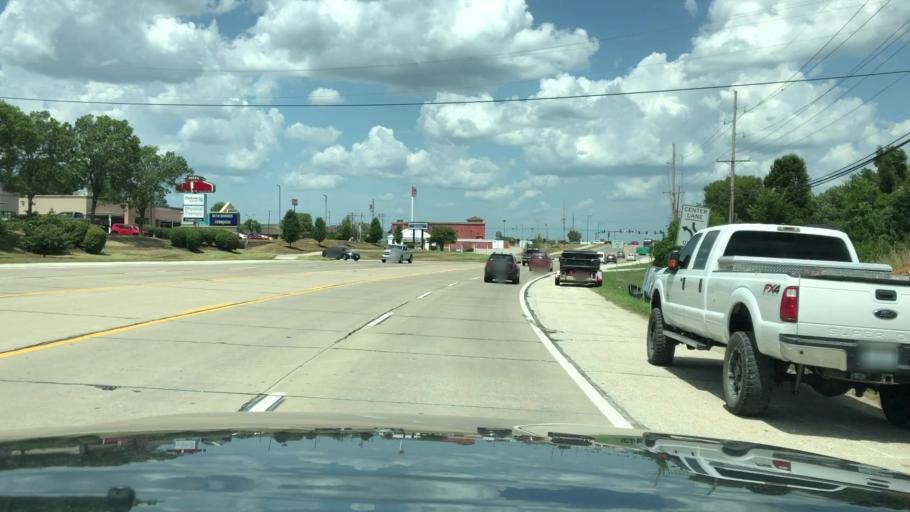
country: US
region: Missouri
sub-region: Saint Charles County
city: O'Fallon
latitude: 38.7968
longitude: -90.7002
